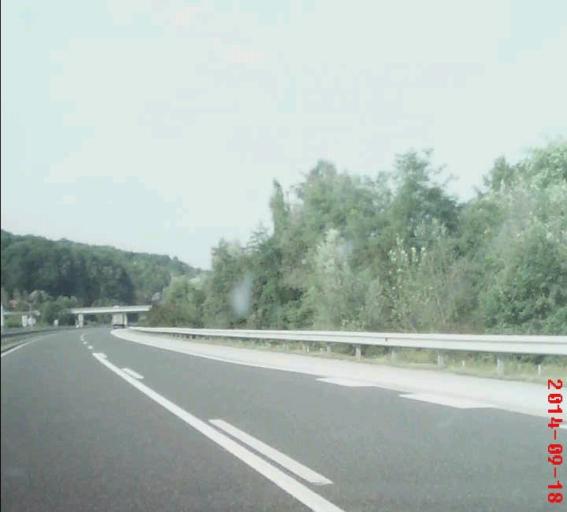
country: SI
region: Pesnica
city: Pesnica pri Mariboru
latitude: 46.6175
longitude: 15.6600
